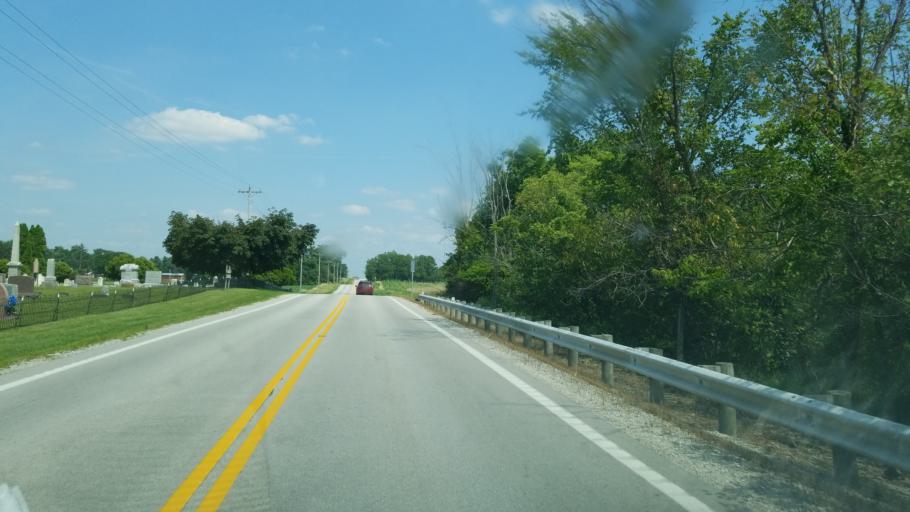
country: US
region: Ohio
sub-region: Sandusky County
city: Mount Carmel
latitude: 41.1248
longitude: -82.9432
